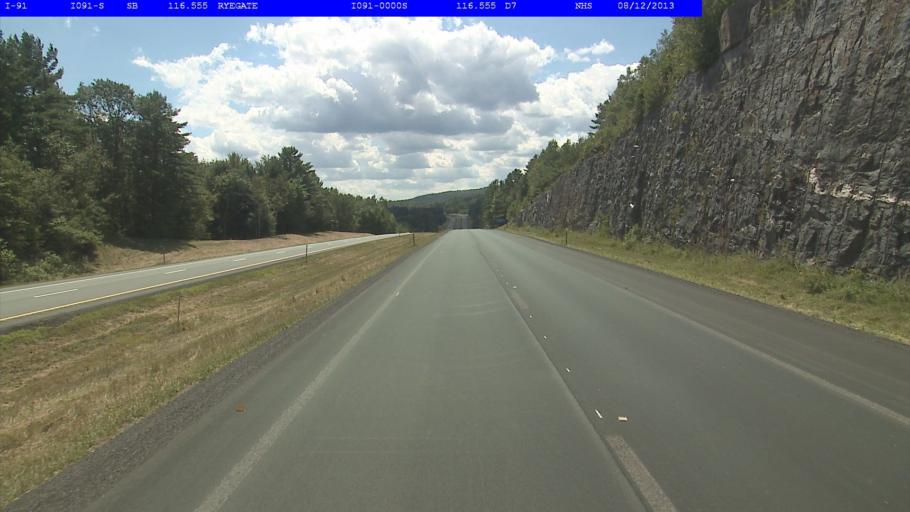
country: US
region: New Hampshire
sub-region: Grafton County
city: Woodsville
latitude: 44.2465
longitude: -72.0625
